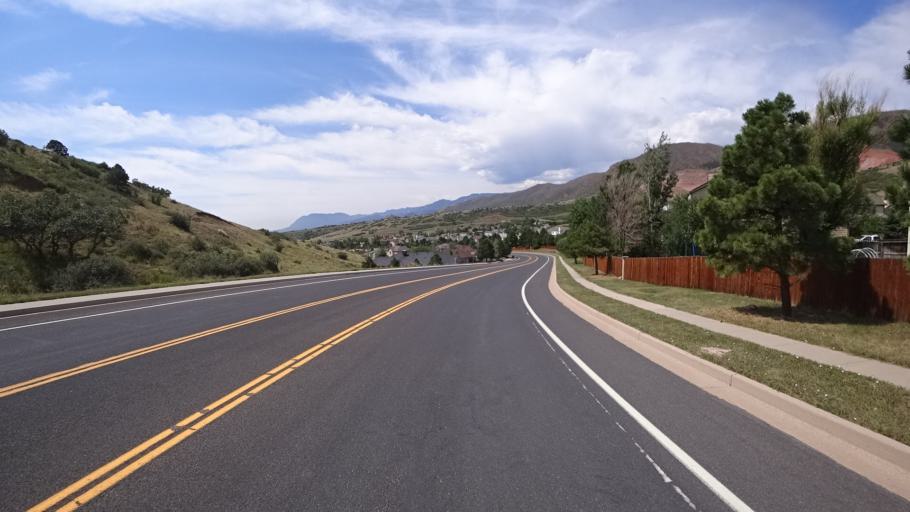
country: US
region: Colorado
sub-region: El Paso County
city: Air Force Academy
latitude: 38.9411
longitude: -104.8751
